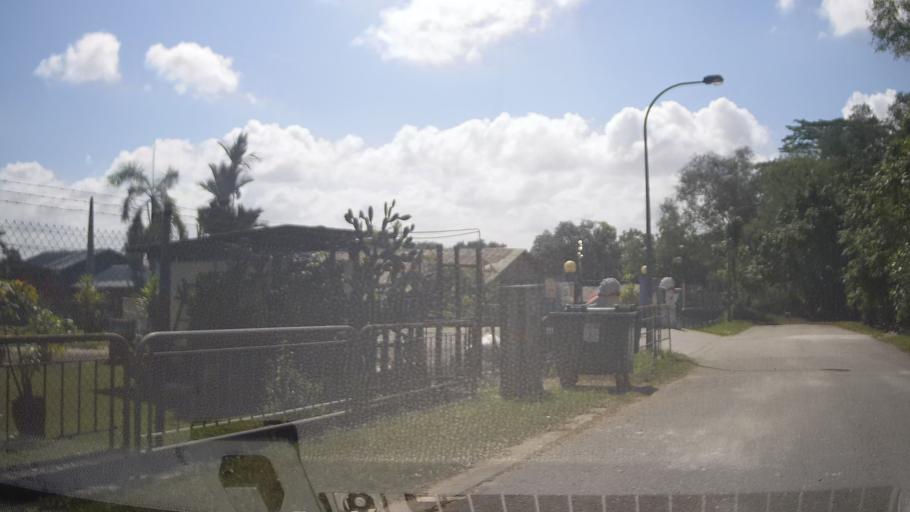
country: MY
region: Johor
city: Johor Bahru
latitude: 1.4324
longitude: 103.7087
